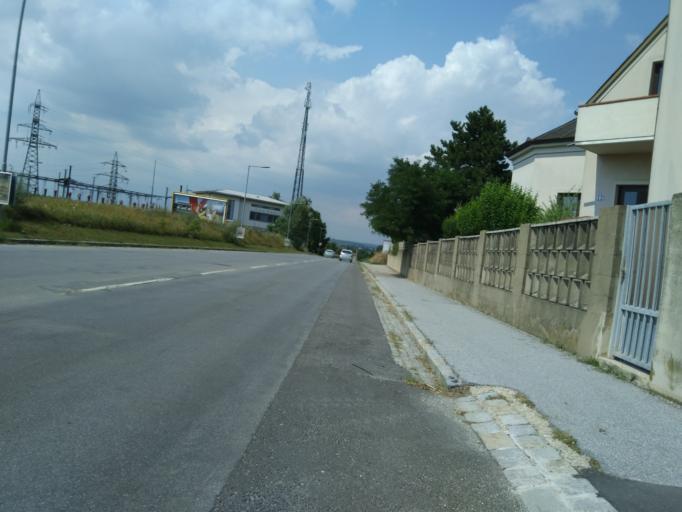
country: AT
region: Lower Austria
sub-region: Politischer Bezirk Ganserndorf
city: Ganserndorf
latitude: 48.3431
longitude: 16.7149
